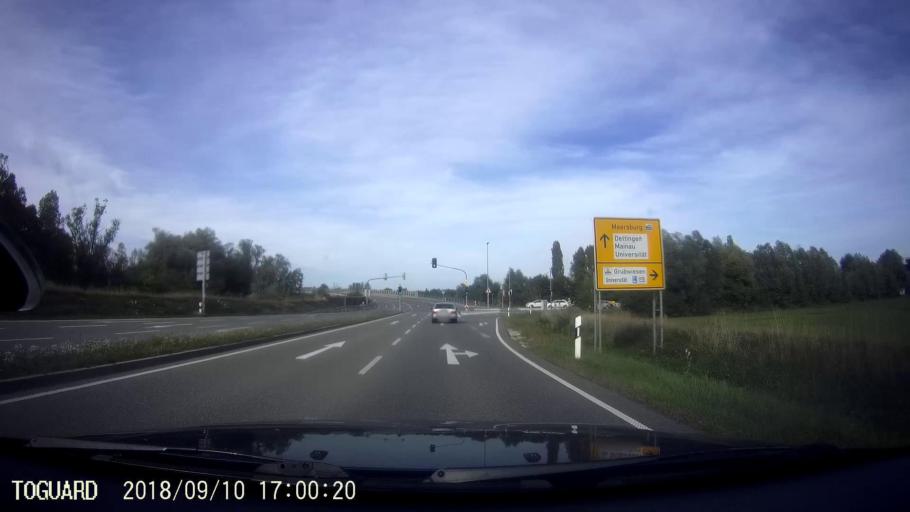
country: CH
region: Thurgau
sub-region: Kreuzlingen District
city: Gottlieben
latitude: 47.6850
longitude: 9.1312
